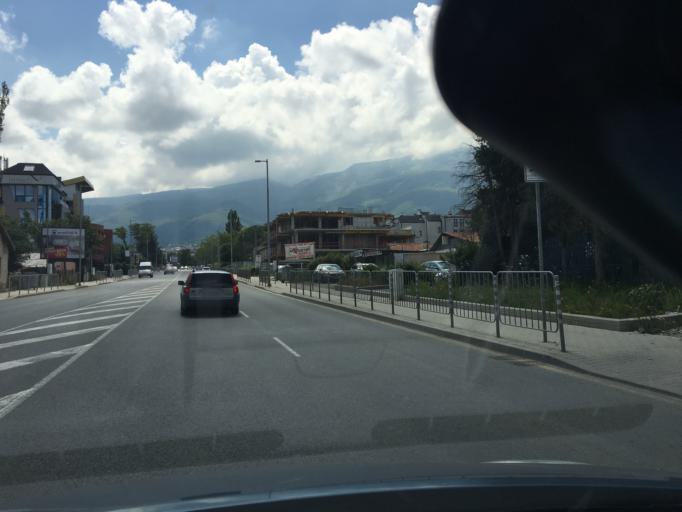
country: BG
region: Sofia-Capital
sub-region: Stolichna Obshtina
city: Sofia
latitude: 42.6477
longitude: 23.3149
